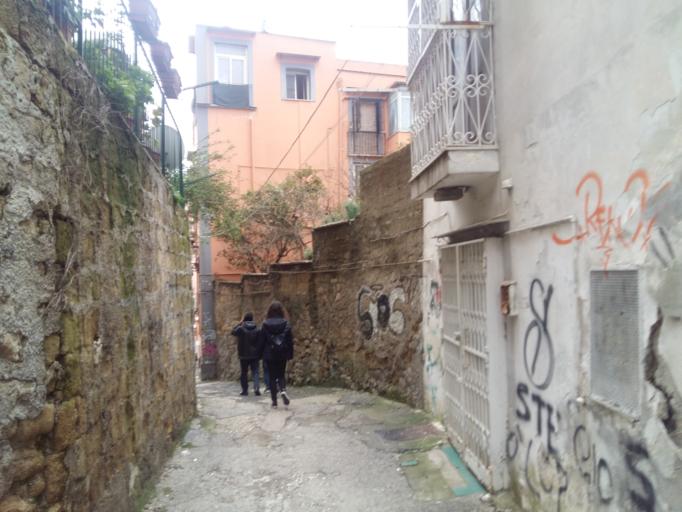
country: IT
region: Campania
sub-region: Provincia di Napoli
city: Napoli
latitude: 40.8565
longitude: 14.2297
